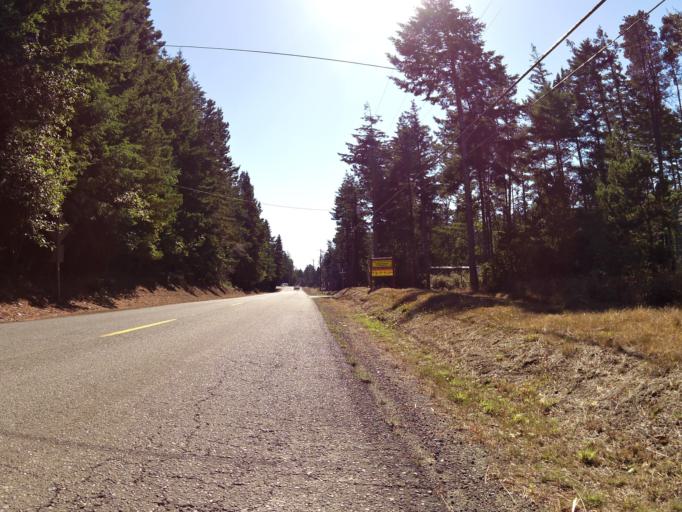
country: US
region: Oregon
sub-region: Coos County
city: Bandon
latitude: 43.1757
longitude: -124.3718
